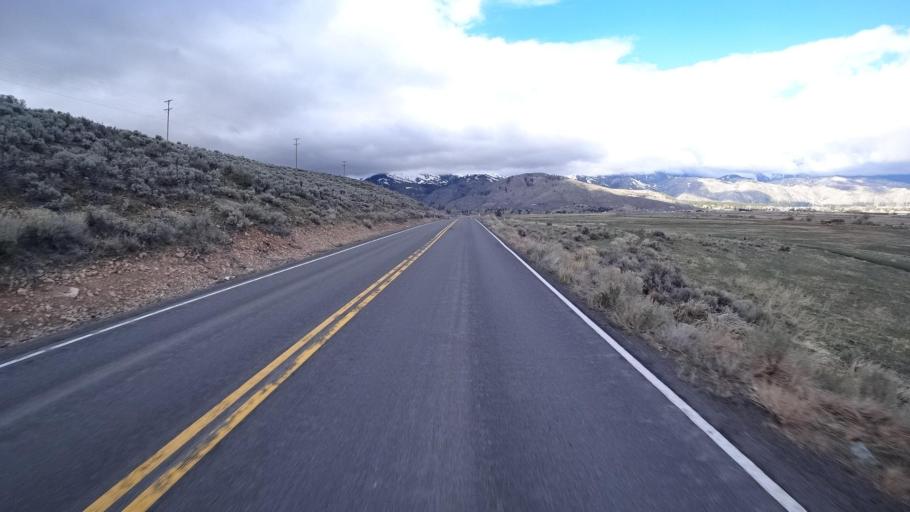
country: US
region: Nevada
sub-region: Carson City
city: Carson City
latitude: 39.2279
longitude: -119.7894
